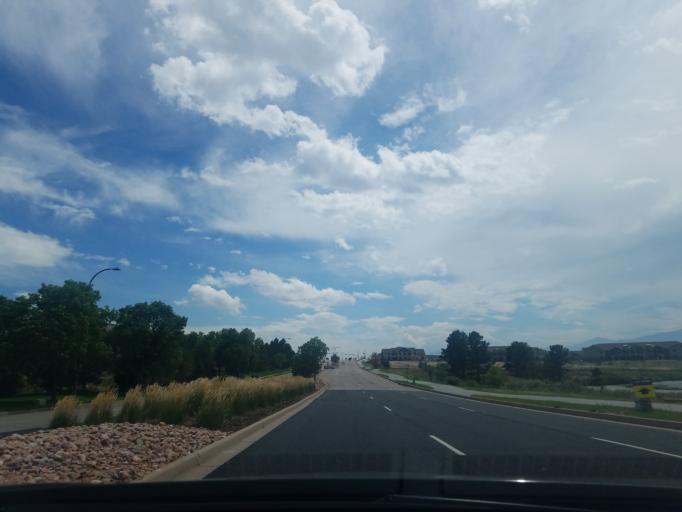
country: US
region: Colorado
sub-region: El Paso County
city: Gleneagle
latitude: 38.9994
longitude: -104.7980
